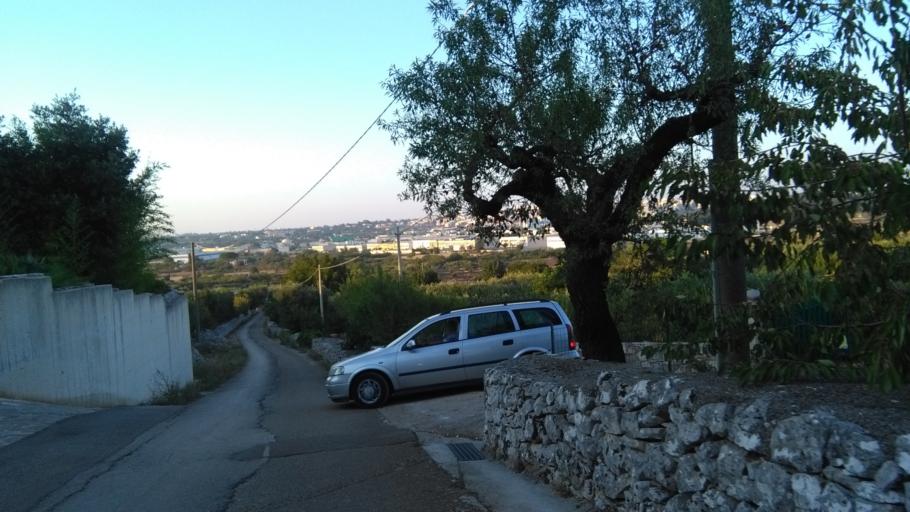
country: IT
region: Apulia
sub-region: Provincia di Bari
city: Putignano
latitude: 40.8261
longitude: 17.1036
